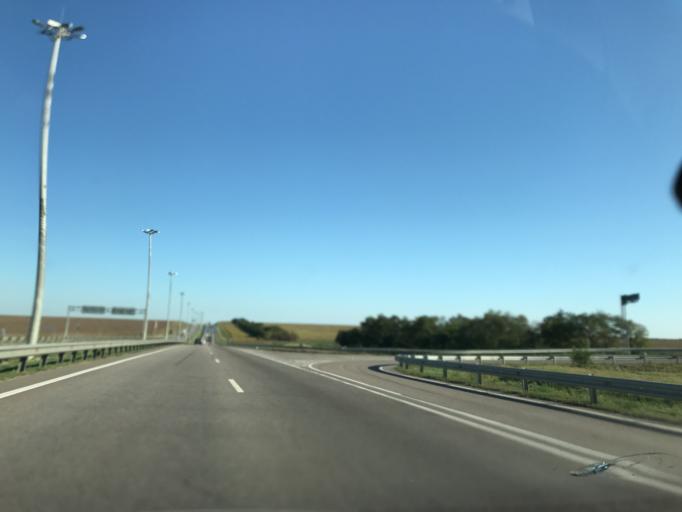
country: RU
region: Rostov
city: Glubokiy
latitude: 48.4521
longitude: 40.3409
